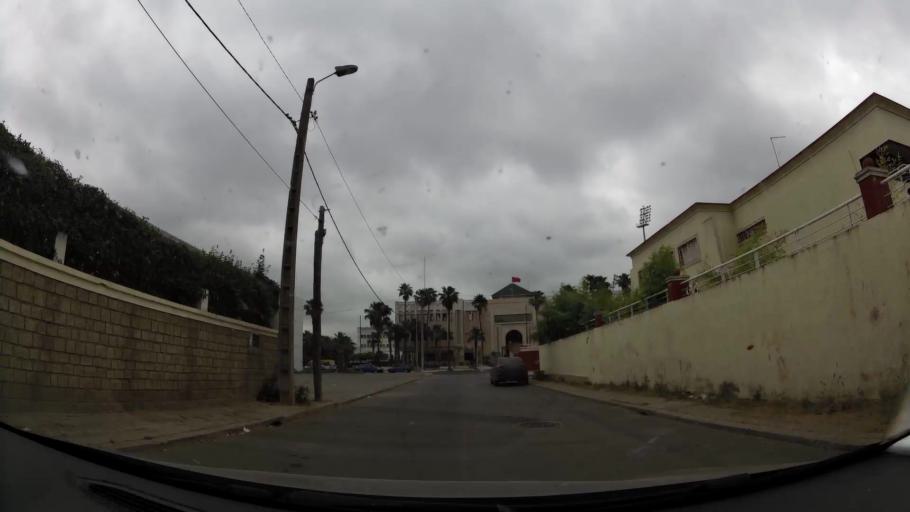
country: MA
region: Rabat-Sale-Zemmour-Zaer
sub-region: Rabat
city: Rabat
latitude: 33.9768
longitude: -6.8261
